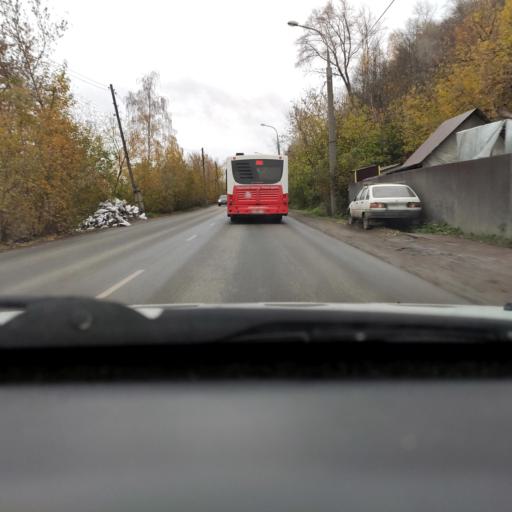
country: RU
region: Perm
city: Perm
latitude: 58.0509
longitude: 56.3272
